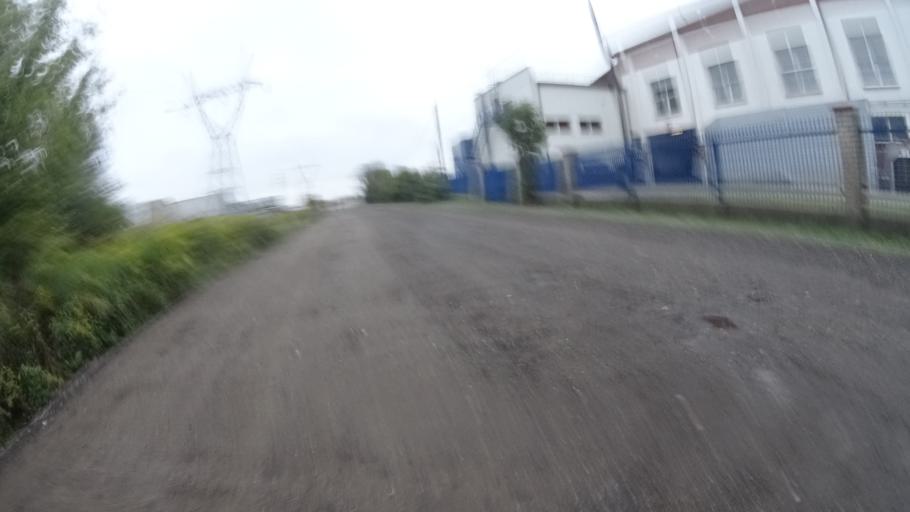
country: PL
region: Masovian Voivodeship
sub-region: Powiat warszawski zachodni
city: Babice
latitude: 52.2246
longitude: 20.8659
